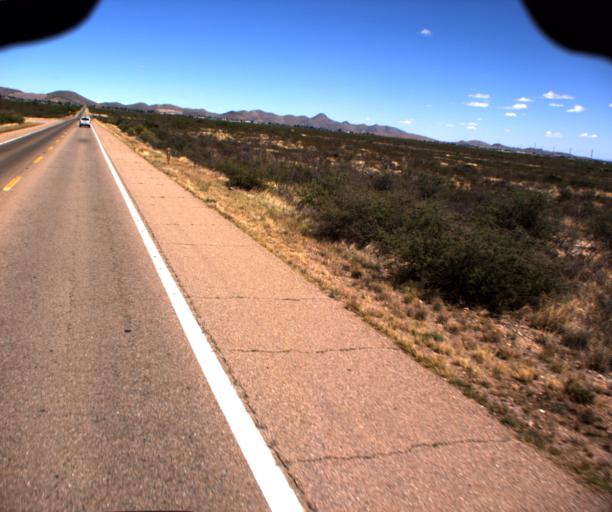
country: US
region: Arizona
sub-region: Cochise County
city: Naco
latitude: 31.3814
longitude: -109.9586
